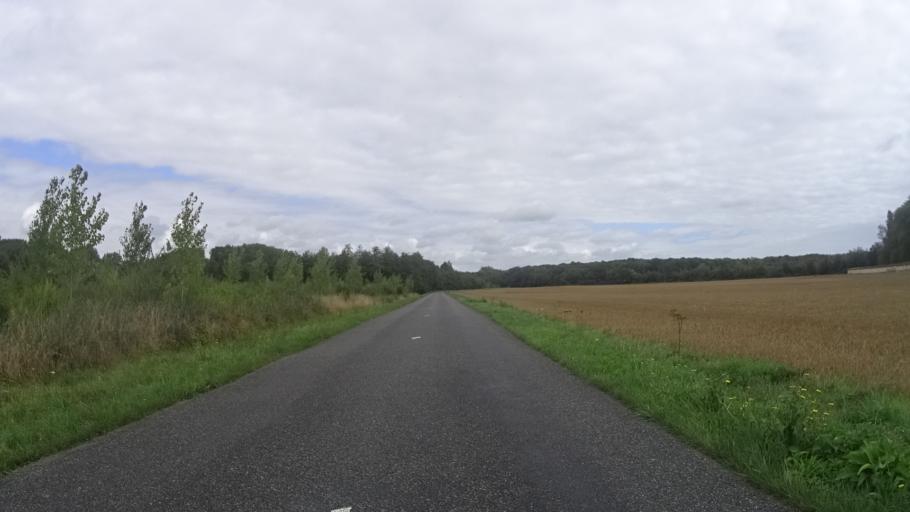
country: FR
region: Picardie
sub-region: Departement de l'Oise
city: Chiry-Ourscamp
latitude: 49.5362
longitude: 2.9720
